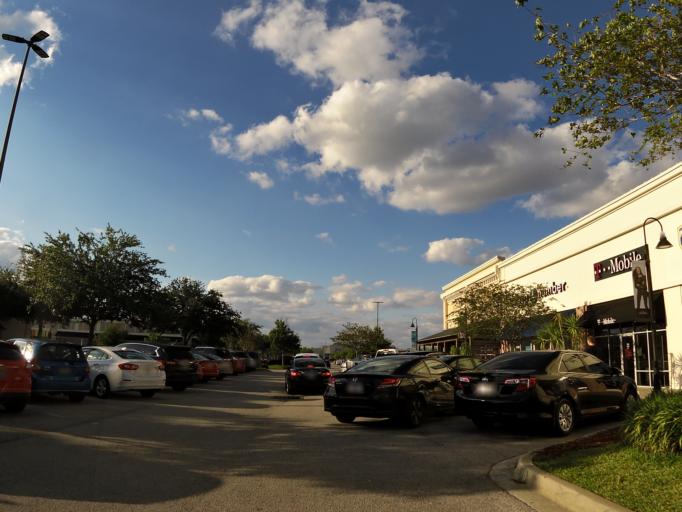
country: US
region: Florida
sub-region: Duval County
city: Jacksonville Beach
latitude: 30.2584
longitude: -81.5270
